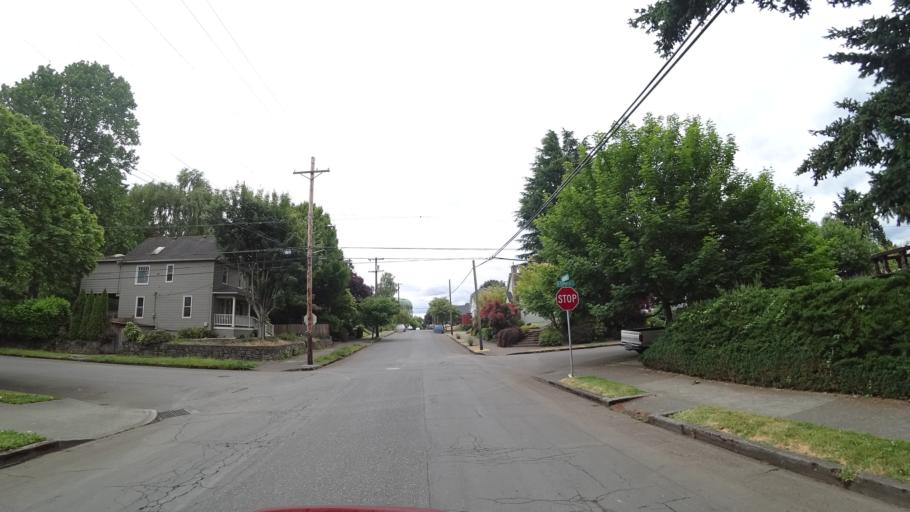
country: US
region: Oregon
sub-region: Multnomah County
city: Portland
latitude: 45.5607
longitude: -122.6875
